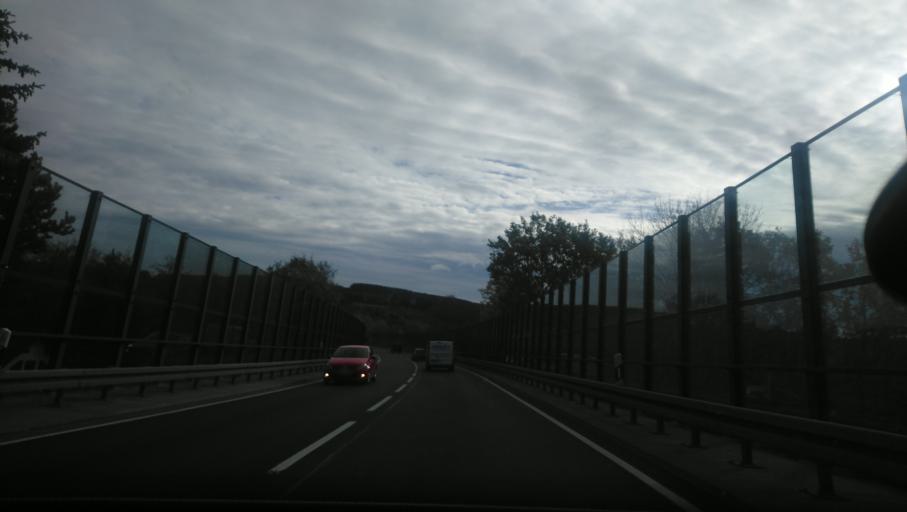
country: DE
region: Saxony
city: Stollberg
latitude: 50.6981
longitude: 12.7707
